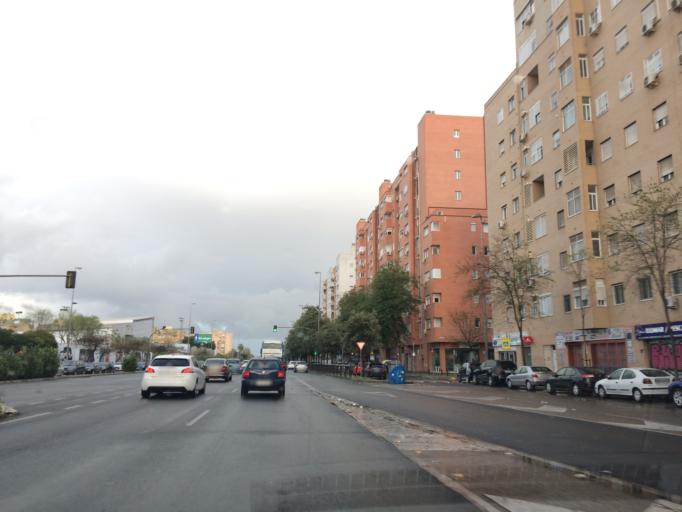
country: ES
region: Andalusia
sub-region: Provincia de Sevilla
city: Sevilla
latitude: 37.4166
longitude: -5.9703
